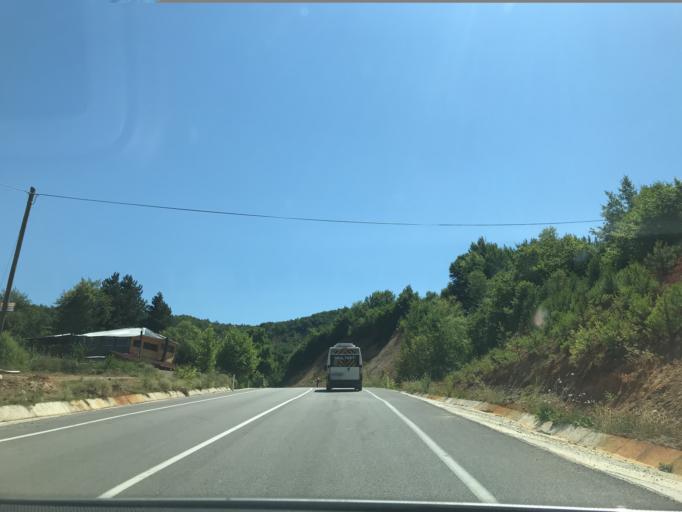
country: TR
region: Bursa
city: Tahtakopru
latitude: 39.9428
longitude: 29.5972
